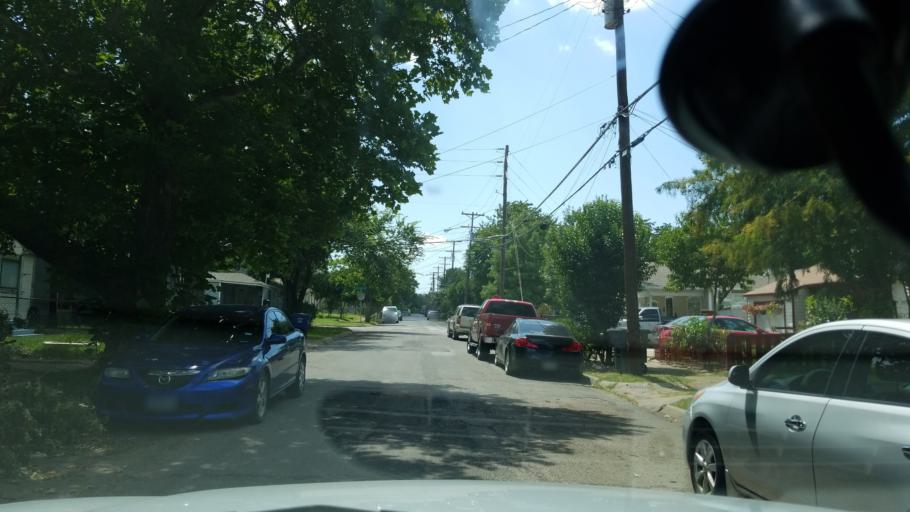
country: US
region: Texas
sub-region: Dallas County
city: Cockrell Hill
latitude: 32.7311
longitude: -96.8788
